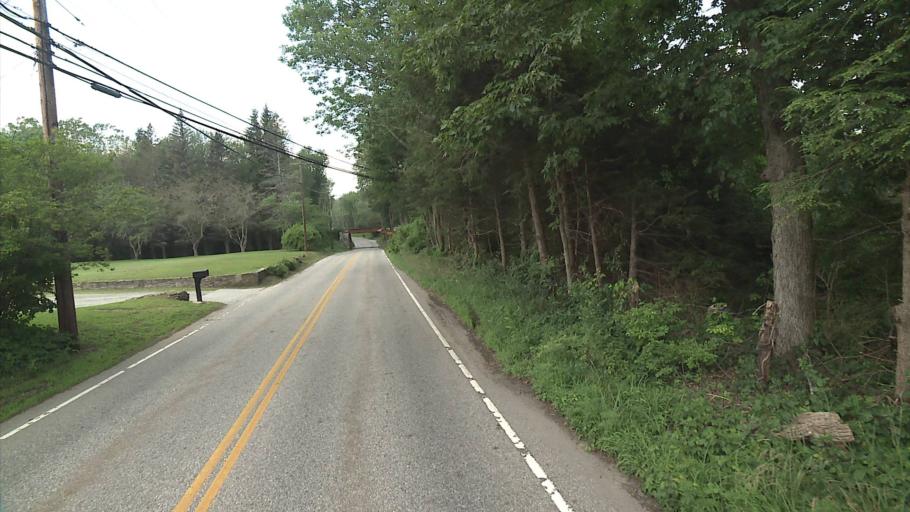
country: US
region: Connecticut
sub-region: New London County
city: Lisbon
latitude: 41.6053
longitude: -72.0022
